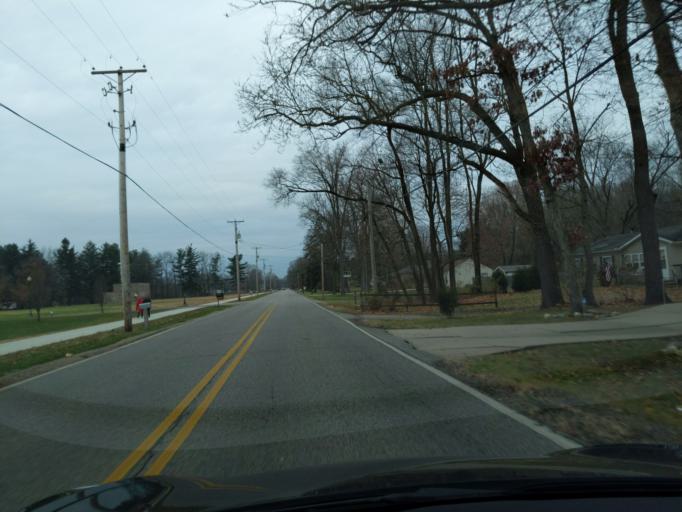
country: US
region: Indiana
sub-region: Saint Joseph County
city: Georgetown
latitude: 41.7325
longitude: -86.2653
